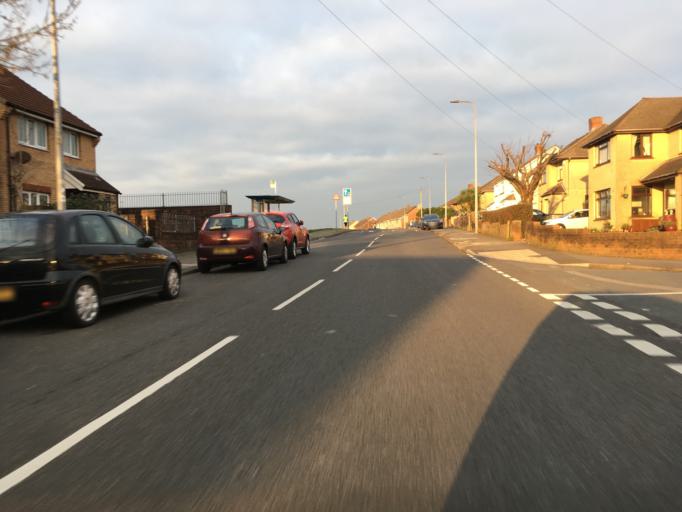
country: GB
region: Wales
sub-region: Newport
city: Marshfield
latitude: 51.5250
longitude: -3.1180
